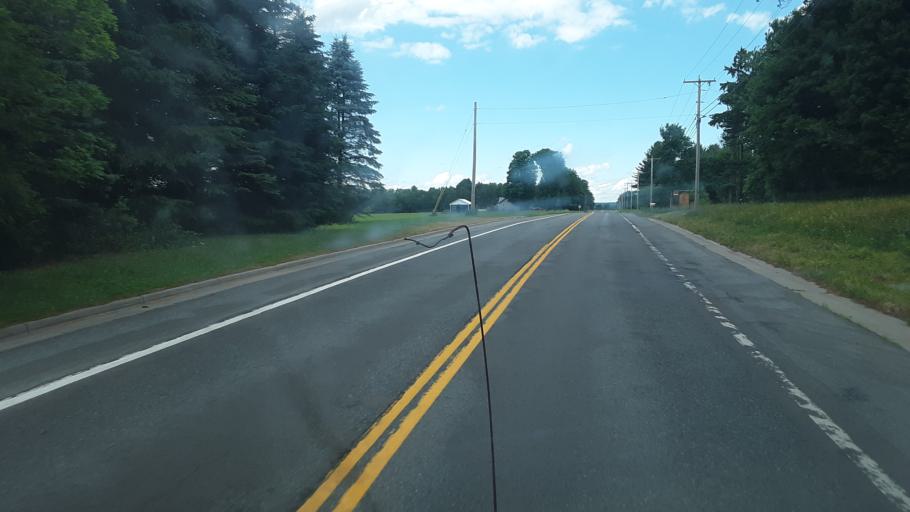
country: US
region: New York
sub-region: Oneida County
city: Rome
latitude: 43.3493
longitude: -75.4763
